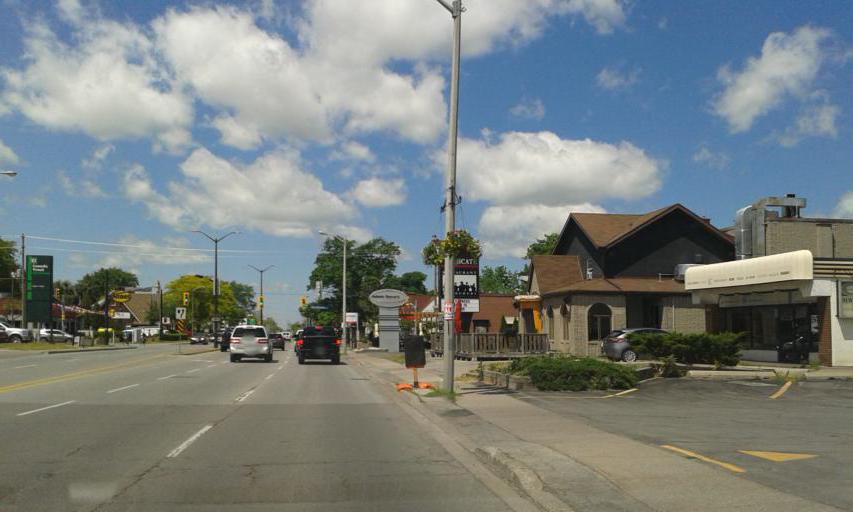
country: CA
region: Ontario
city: Niagara Falls
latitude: 43.0893
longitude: -79.1091
